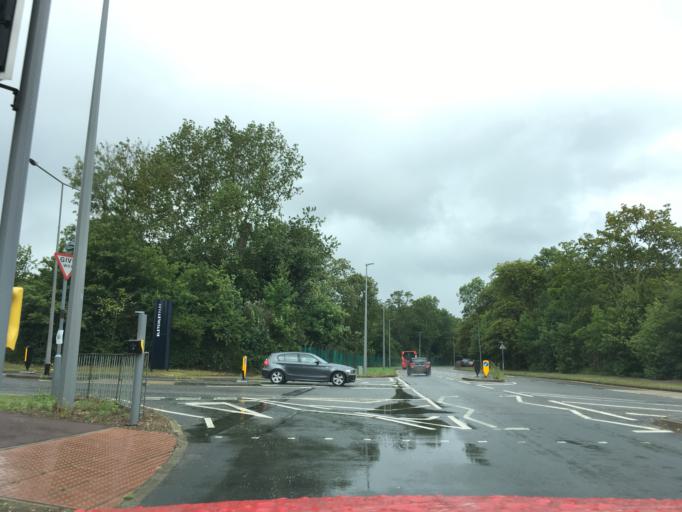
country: GB
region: England
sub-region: Buckinghamshire
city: Bletchley
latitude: 51.9967
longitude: -0.7381
